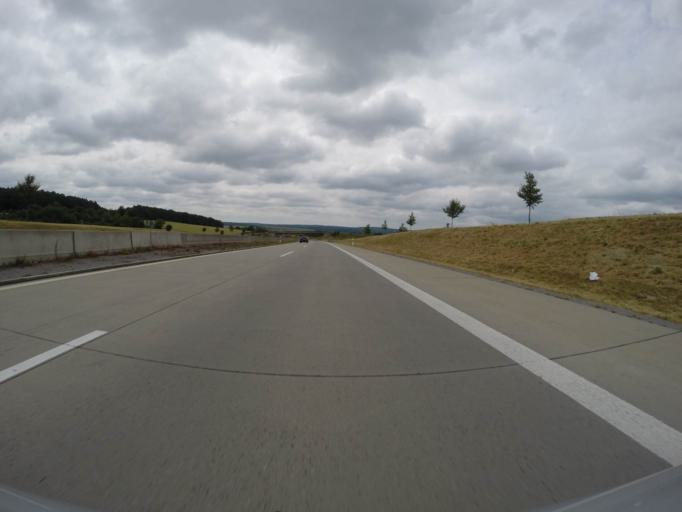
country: DE
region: Bavaria
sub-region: Regierungsbezirk Unterfranken
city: Munnerstadt
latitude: 50.2613
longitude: 10.2190
